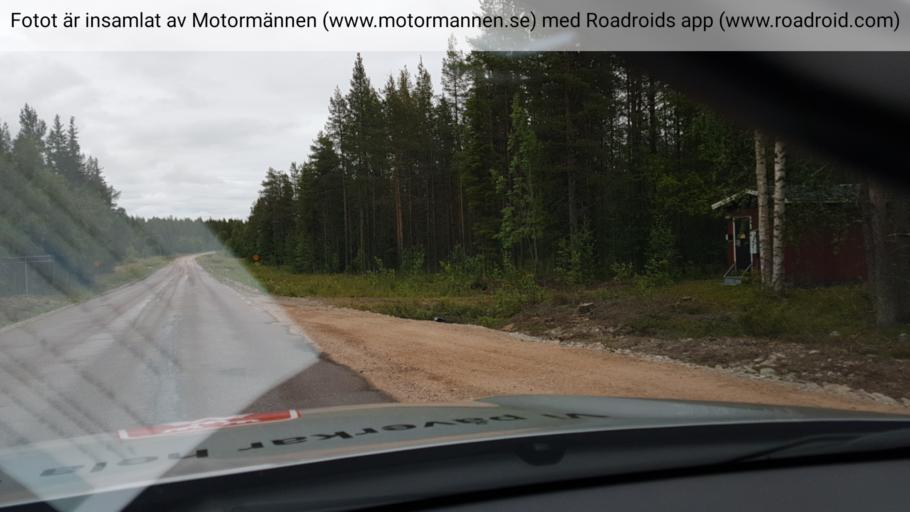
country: SE
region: Norrbotten
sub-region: Overkalix Kommun
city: OEverkalix
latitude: 67.0641
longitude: 22.2568
